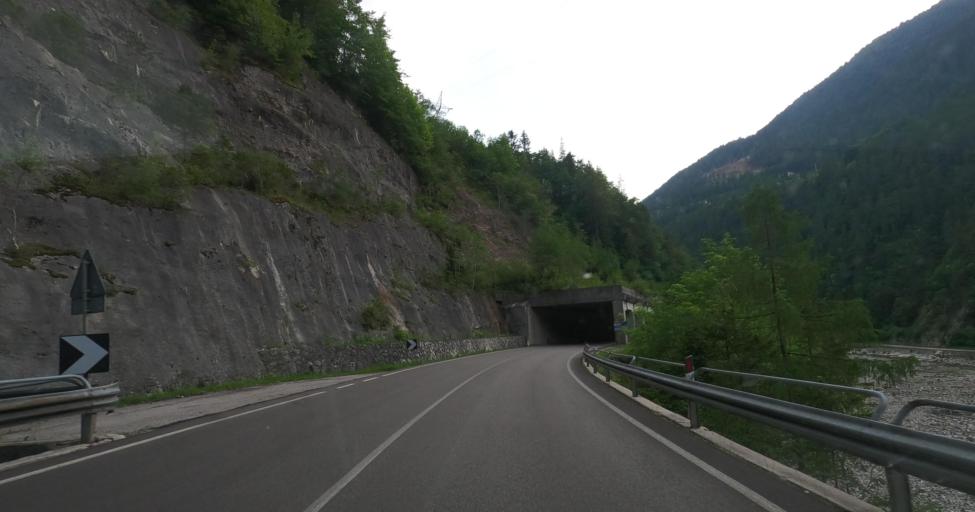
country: IT
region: Veneto
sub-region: Provincia di Belluno
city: Celat-San Tomaso Agordino
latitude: 46.3721
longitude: 11.9810
